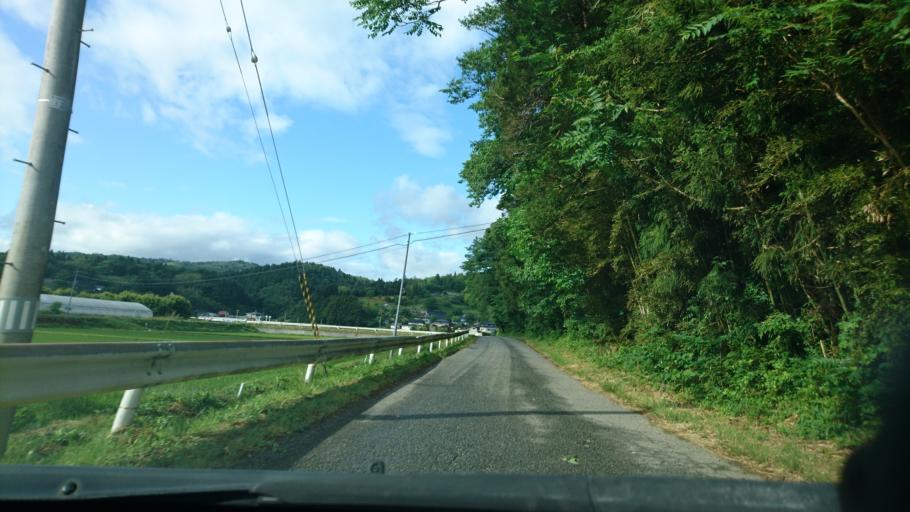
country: JP
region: Iwate
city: Ichinoseki
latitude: 38.8550
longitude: 141.2828
